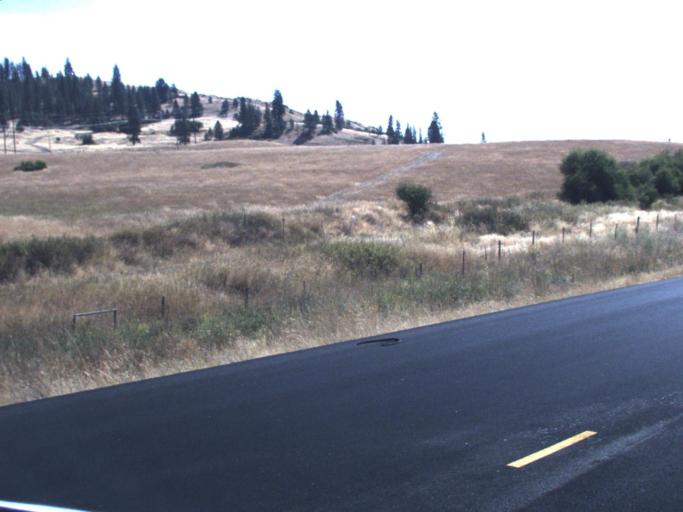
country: US
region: Washington
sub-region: Stevens County
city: Colville
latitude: 48.4952
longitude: -117.9025
